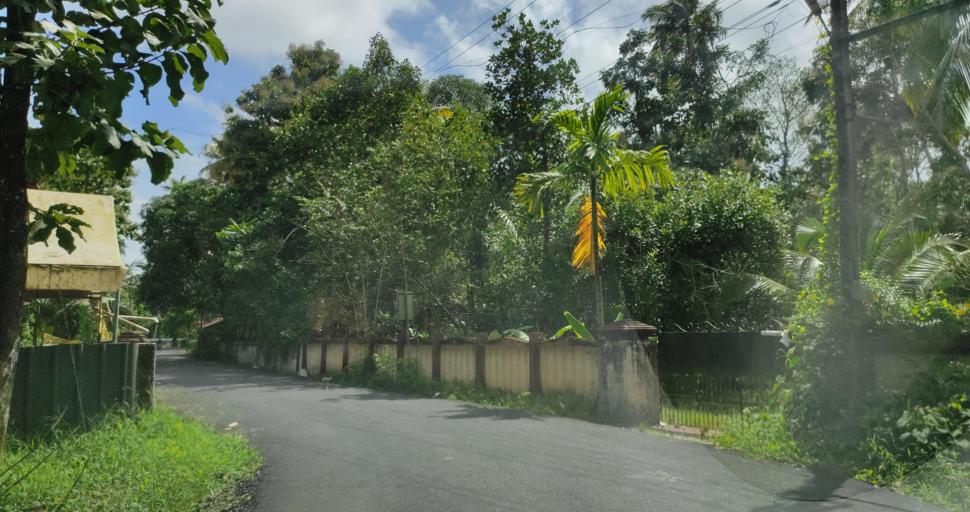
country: IN
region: Kerala
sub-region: Alappuzha
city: Shertallai
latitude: 9.6615
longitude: 76.3731
